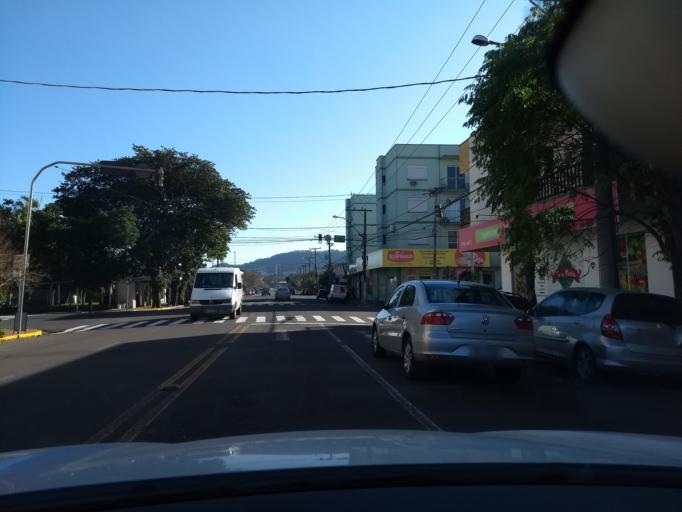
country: BR
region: Rio Grande do Sul
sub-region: Santa Cruz Do Sul
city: Santa Cruz do Sul
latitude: -29.7120
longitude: -52.4356
